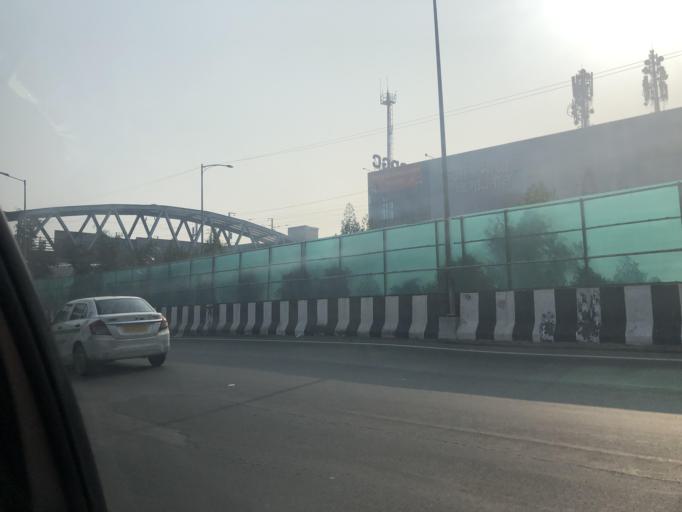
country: IN
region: NCT
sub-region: Central Delhi
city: Karol Bagh
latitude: 28.5925
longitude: 77.1617
